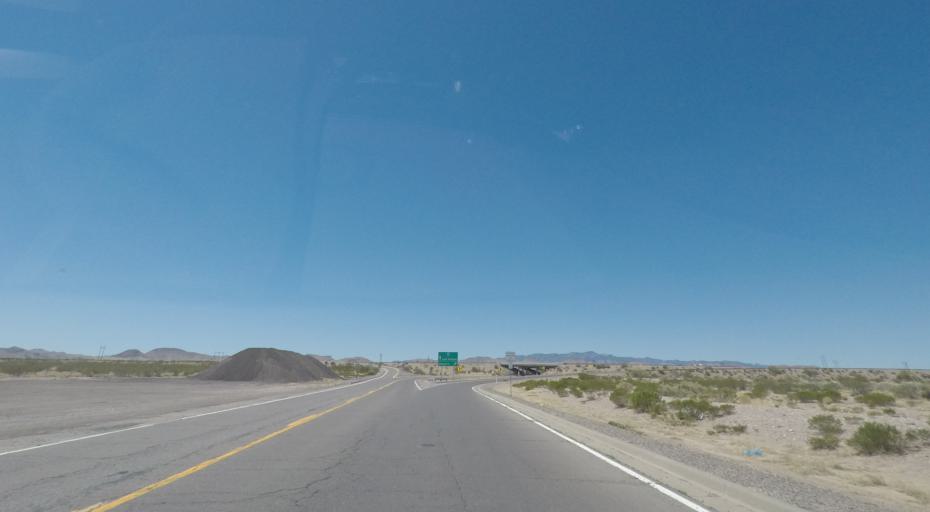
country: US
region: New Mexico
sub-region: Socorro County
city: Socorro
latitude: 33.9173
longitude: -106.8755
